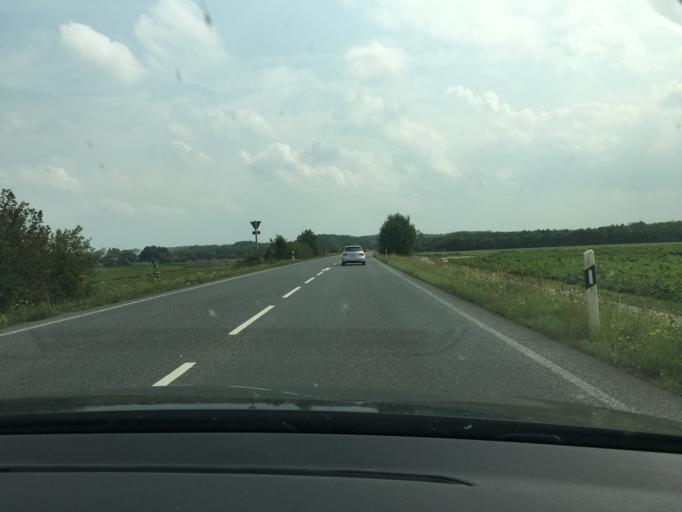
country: DE
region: North Rhine-Westphalia
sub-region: Regierungsbezirk Koln
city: Norvenich
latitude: 50.8470
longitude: 6.6188
